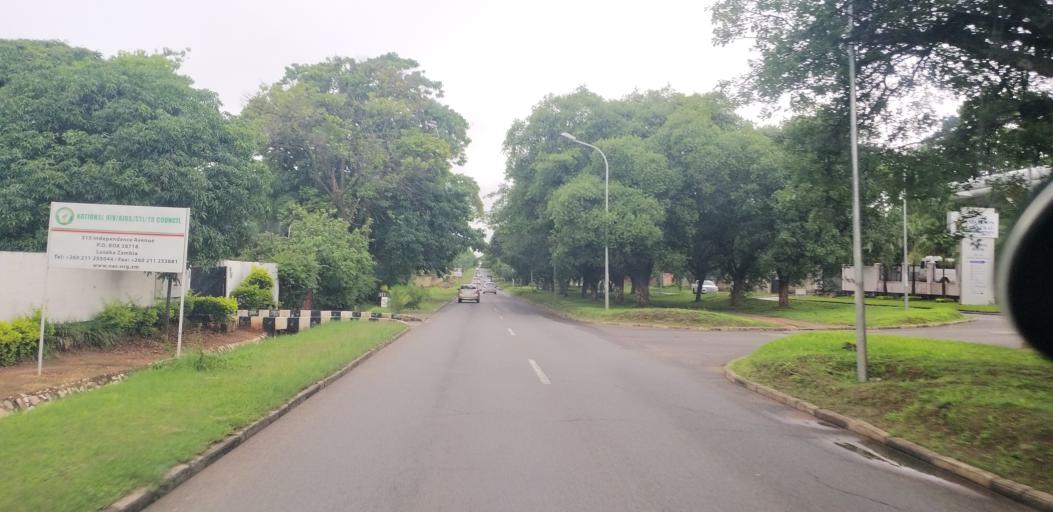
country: ZM
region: Lusaka
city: Lusaka
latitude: -15.4259
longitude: 28.3144
